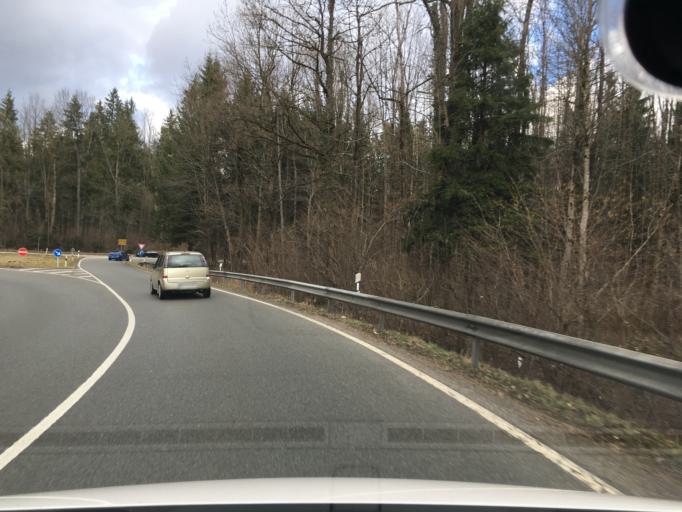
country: DE
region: Bavaria
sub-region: Upper Bavaria
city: Rosenheim
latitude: 47.8426
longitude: 12.1402
